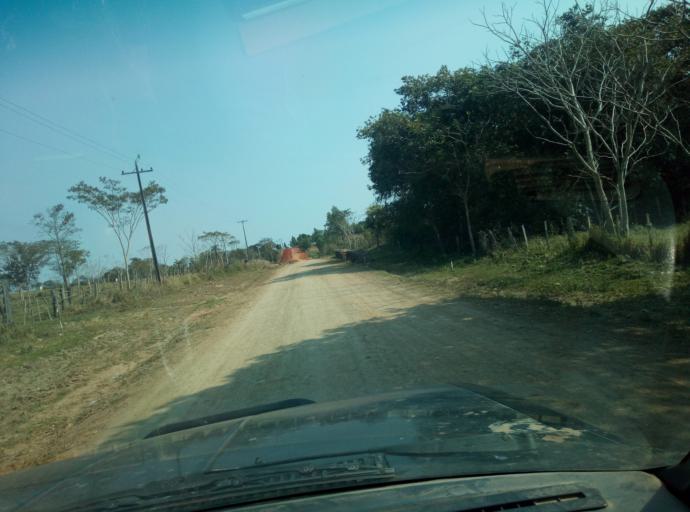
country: PY
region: Caaguazu
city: Coronel Oviedo
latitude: -25.3290
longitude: -56.3257
